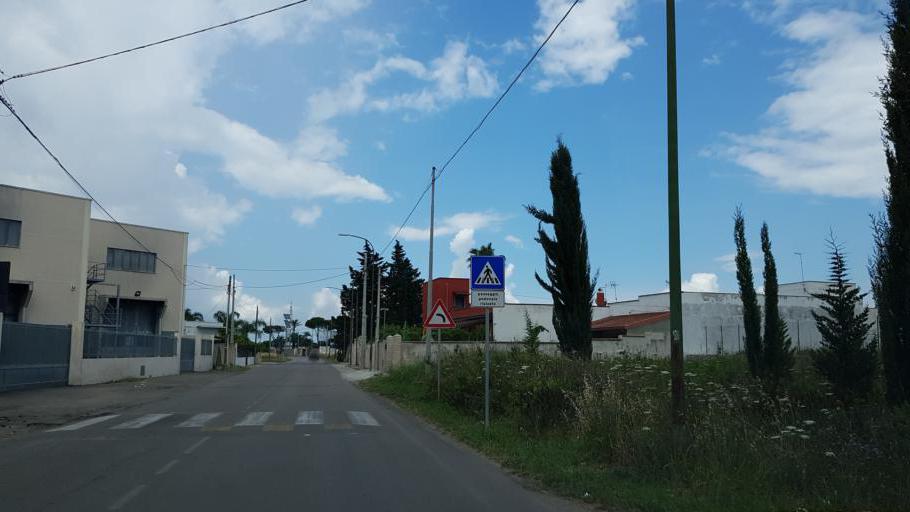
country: IT
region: Apulia
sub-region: Provincia di Brindisi
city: San Donaci
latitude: 40.4555
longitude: 17.9220
